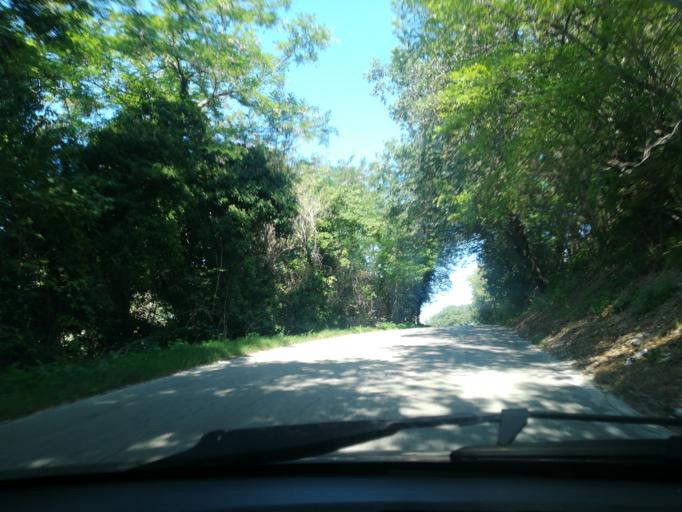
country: IT
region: The Marches
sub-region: Provincia di Macerata
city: Sforzacosta
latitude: 43.2663
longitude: 13.4526
